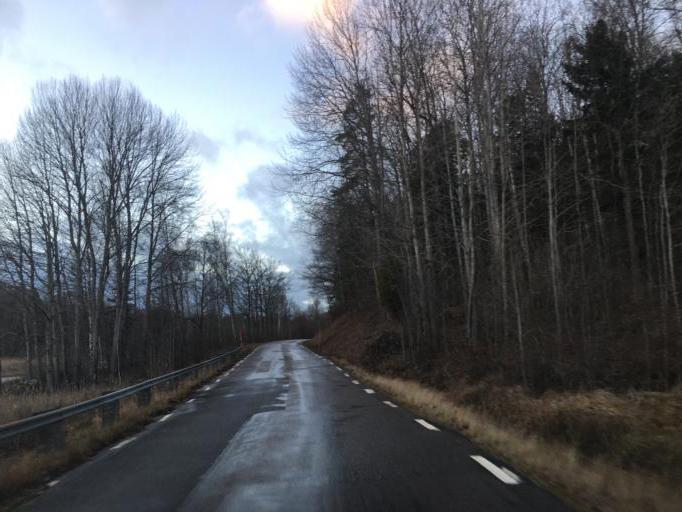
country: SE
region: Kalmar
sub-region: Vasterviks Kommun
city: Ankarsrum
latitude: 57.5695
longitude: 16.4955
